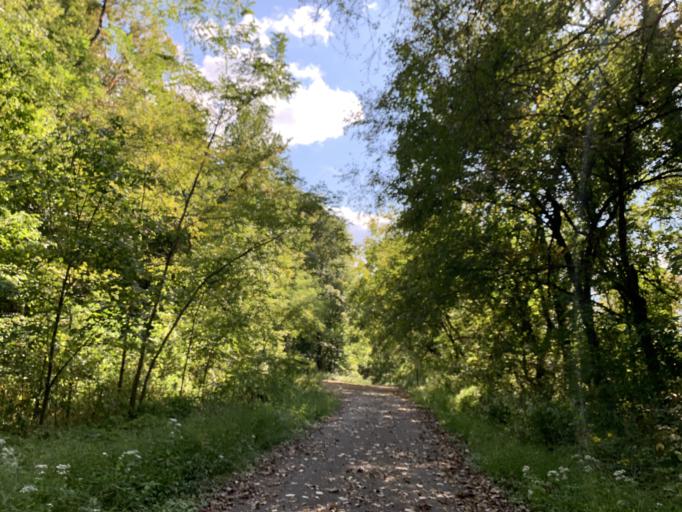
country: US
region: Indiana
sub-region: Floyd County
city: New Albany
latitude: 38.2589
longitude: -85.8318
